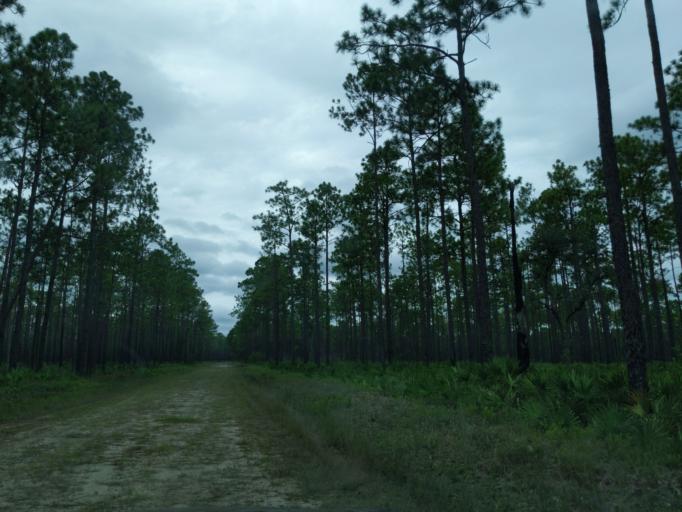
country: US
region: Florida
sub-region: Gadsden County
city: Midway
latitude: 30.3798
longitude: -84.4898
